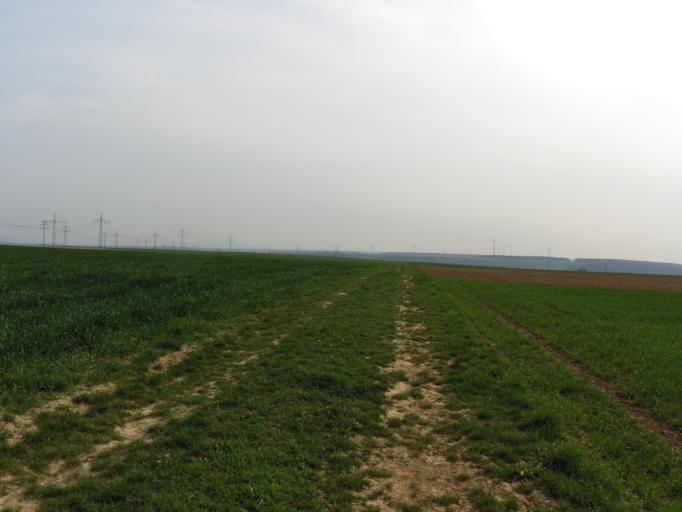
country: DE
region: Bavaria
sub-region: Regierungsbezirk Unterfranken
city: Theilheim
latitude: 49.7729
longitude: 10.0373
